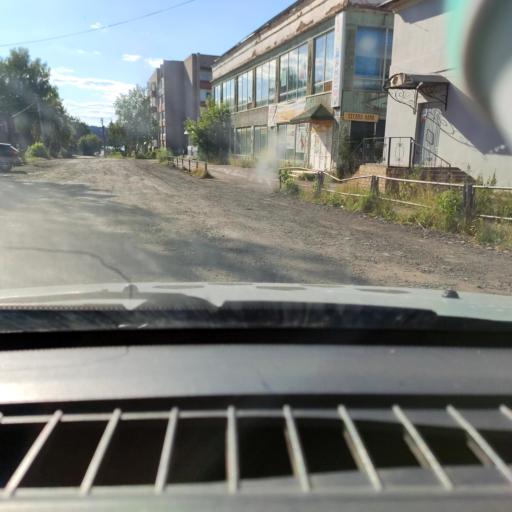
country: RU
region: Perm
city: Ocher
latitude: 57.8839
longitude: 54.7139
